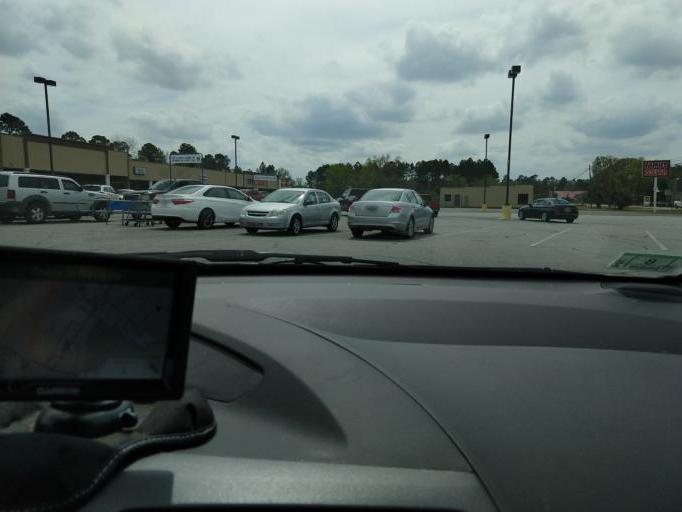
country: US
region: South Carolina
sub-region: Orangeburg County
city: Holly Hill
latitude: 33.4838
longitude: -80.4788
